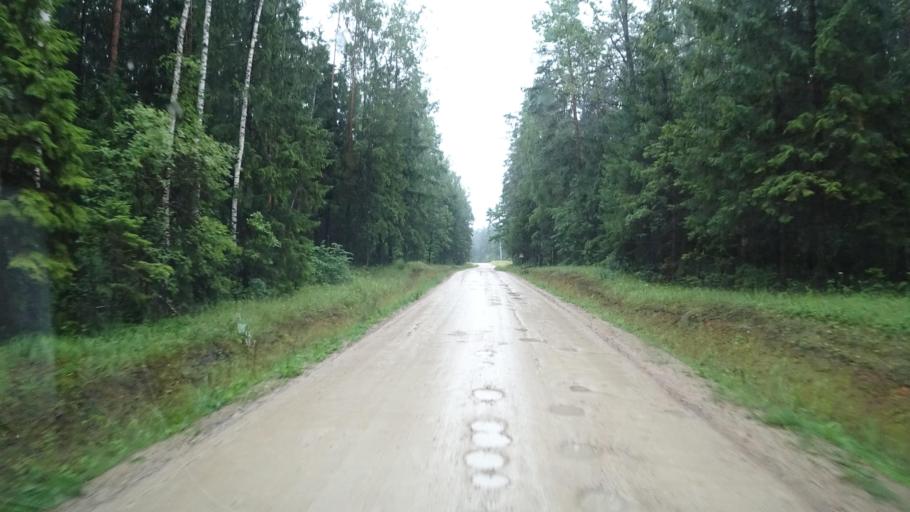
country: LV
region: Lecava
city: Iecava
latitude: 56.6449
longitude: 24.1735
